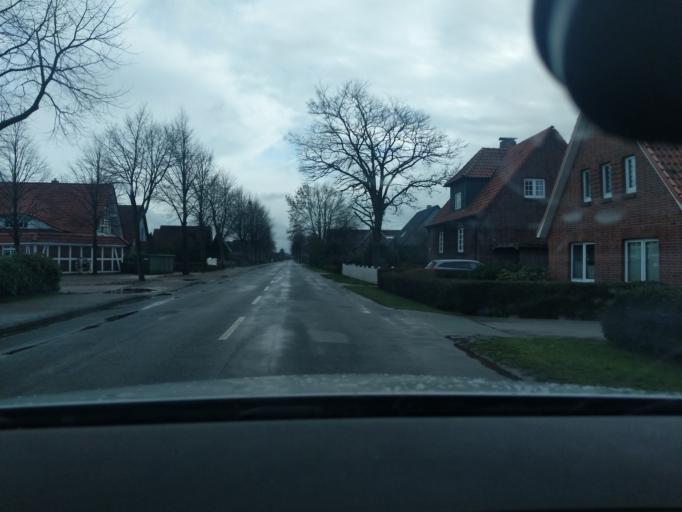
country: DE
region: Lower Saxony
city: Agathenburg
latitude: 53.5990
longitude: 9.5524
